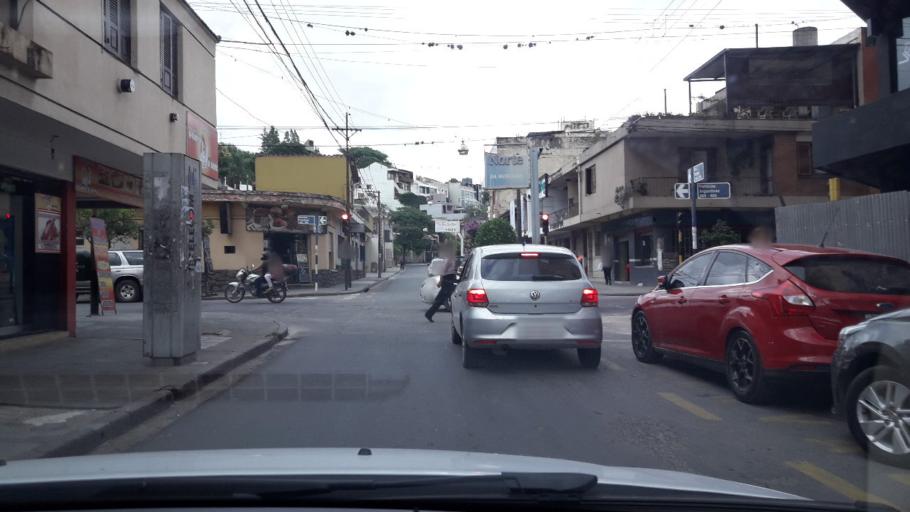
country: AR
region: Jujuy
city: San Salvador de Jujuy
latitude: -24.1857
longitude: -65.3108
